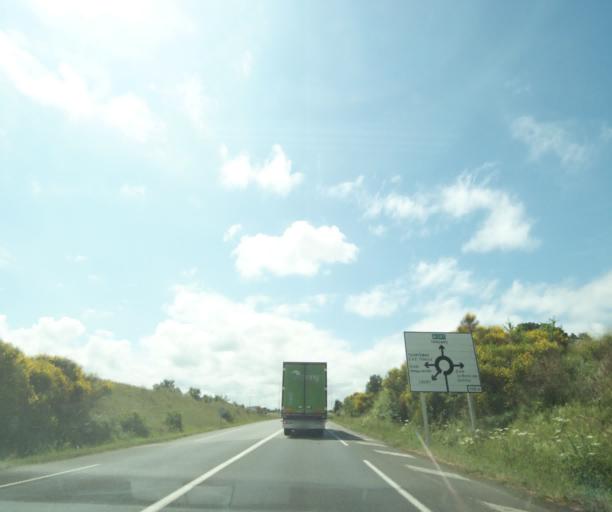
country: FR
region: Poitou-Charentes
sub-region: Departement des Deux-Sevres
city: Louzy
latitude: 47.0007
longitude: -0.1943
